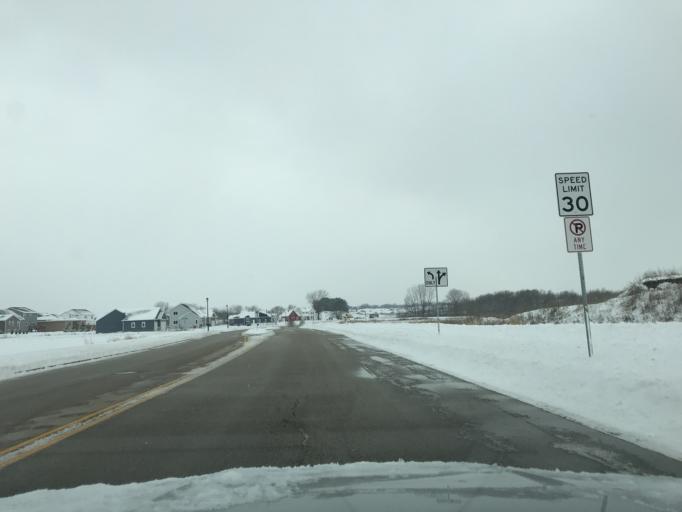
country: US
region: Wisconsin
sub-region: Dane County
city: Sun Prairie
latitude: 43.1763
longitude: -89.2694
